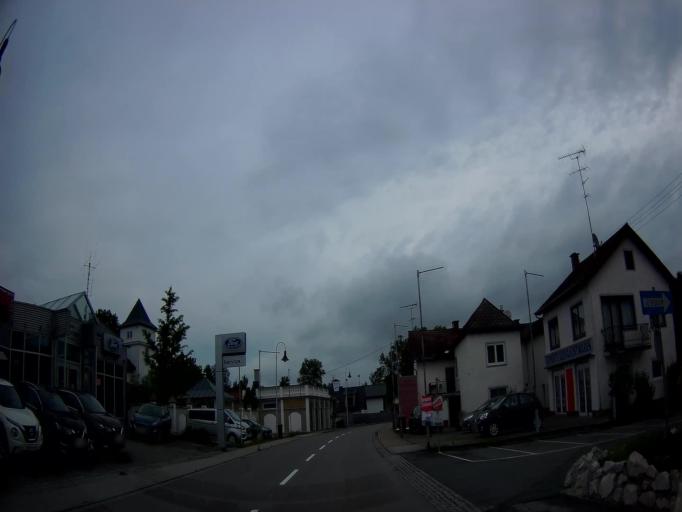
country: AT
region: Salzburg
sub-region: Politischer Bezirk Salzburg-Umgebung
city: Mattsee
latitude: 48.0898
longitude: 13.1487
